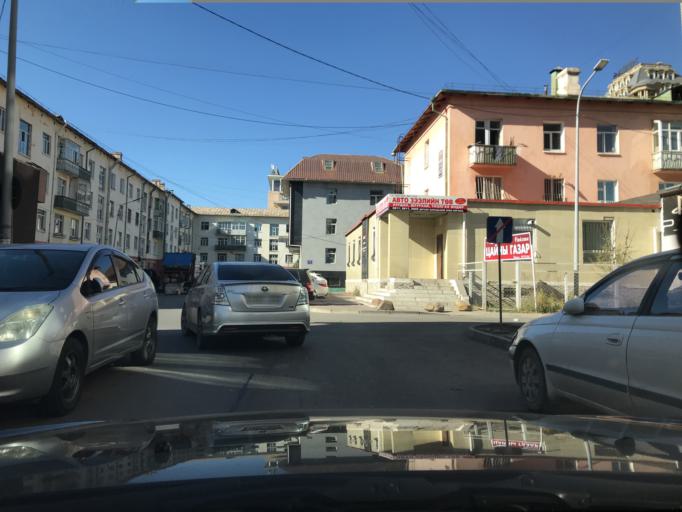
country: MN
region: Ulaanbaatar
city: Ulaanbaatar
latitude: 47.9169
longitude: 106.9091
